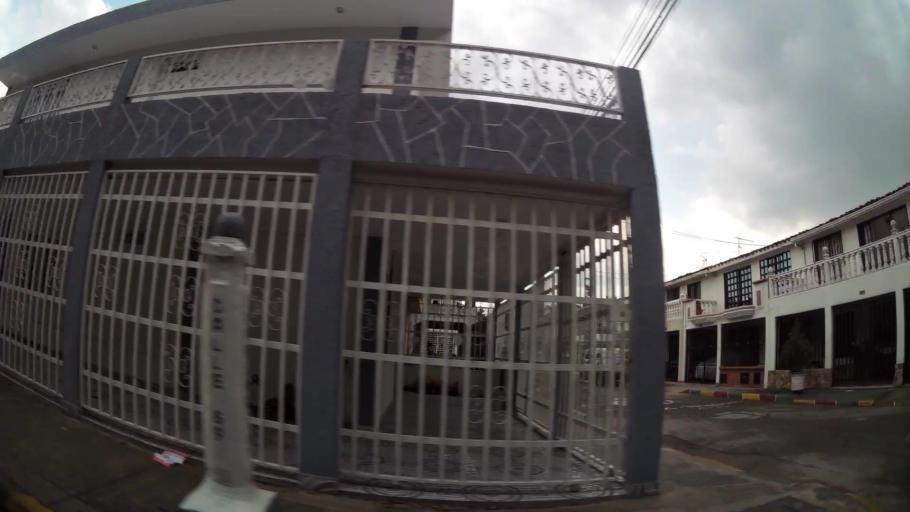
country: CO
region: Valle del Cauca
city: Cali
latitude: 3.4535
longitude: -76.4877
